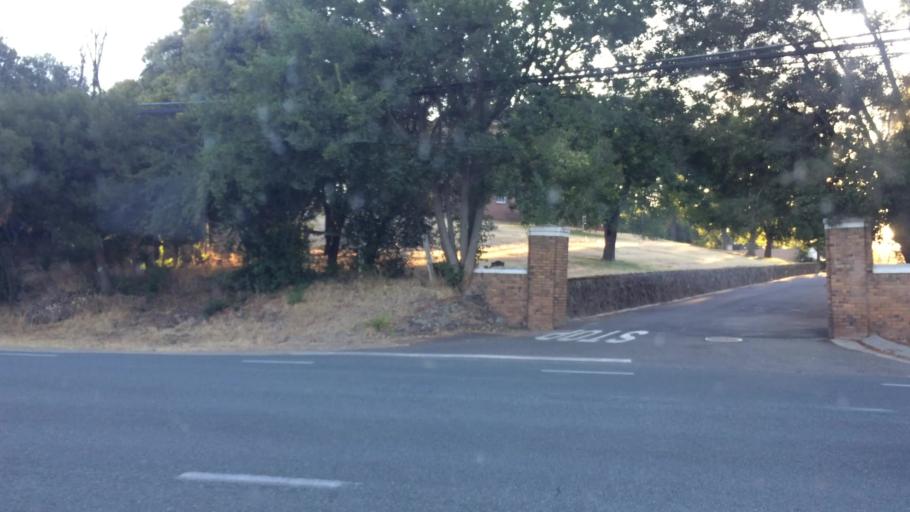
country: US
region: California
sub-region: Amador County
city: Ione
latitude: 38.3590
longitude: -120.9397
